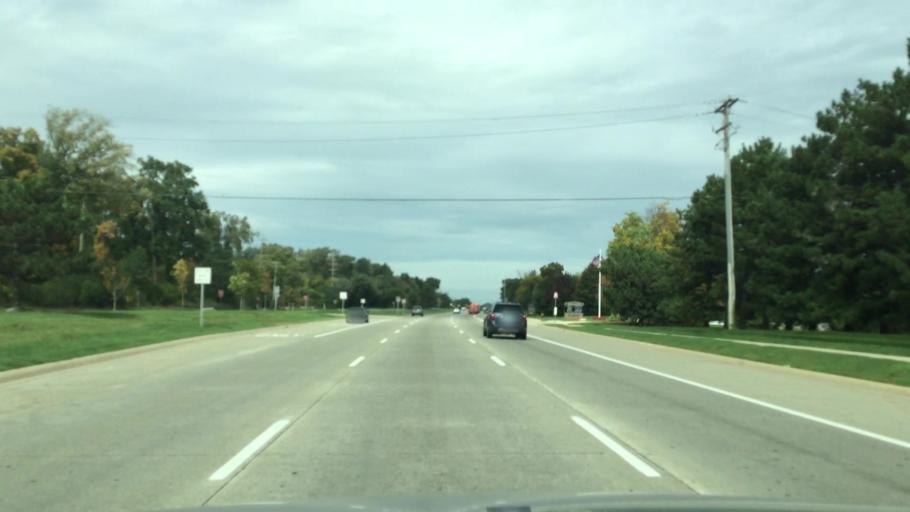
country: US
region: Michigan
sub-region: Oakland County
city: Bingham Farms
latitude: 42.5197
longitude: -83.2858
